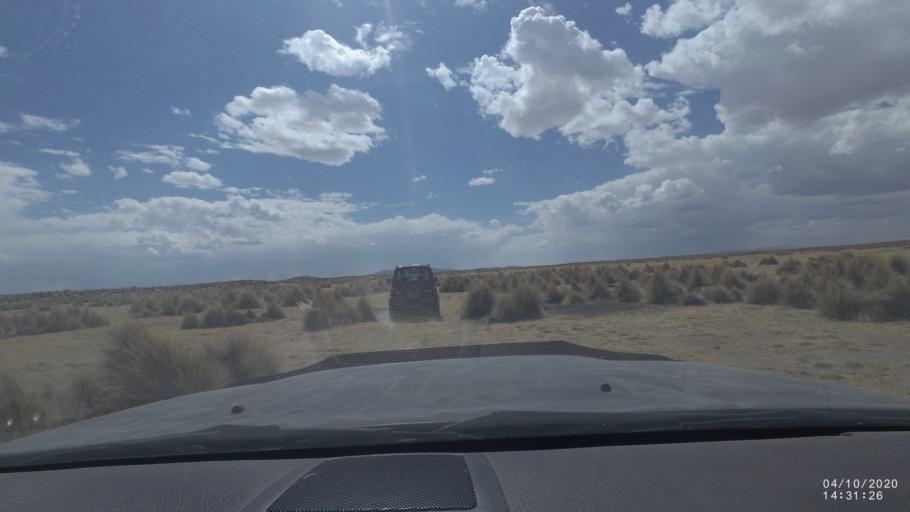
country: BO
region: Oruro
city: Poopo
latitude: -18.6747
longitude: -67.4629
